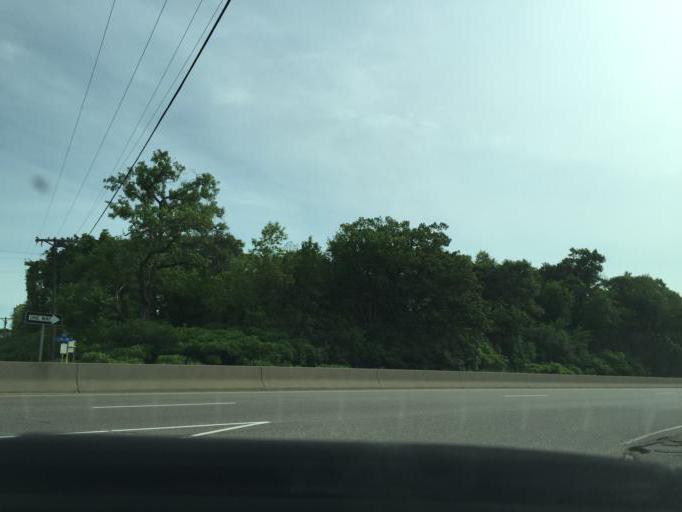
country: US
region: Minnesota
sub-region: Hennepin County
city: Hopkins
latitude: 44.9226
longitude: -93.4627
